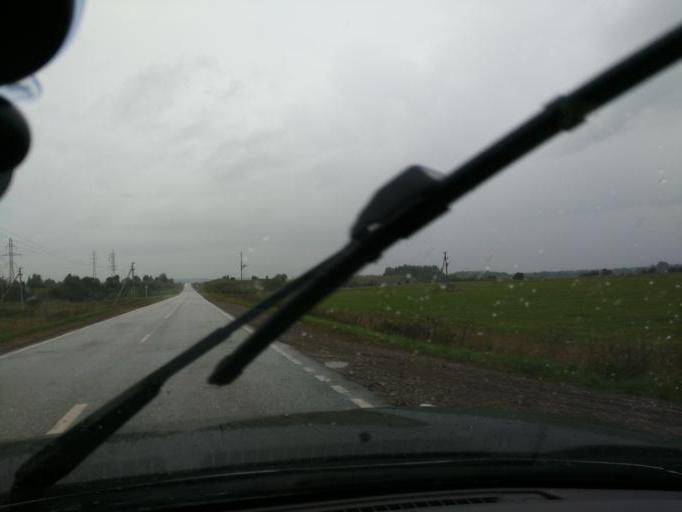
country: RU
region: Perm
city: Barda
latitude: 57.0879
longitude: 55.5390
